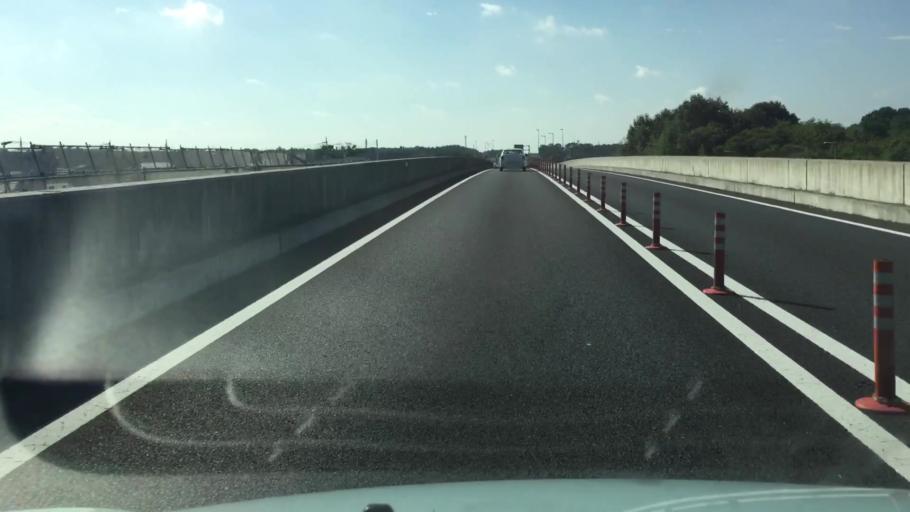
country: JP
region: Tochigi
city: Mooka
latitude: 36.5108
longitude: 139.9870
